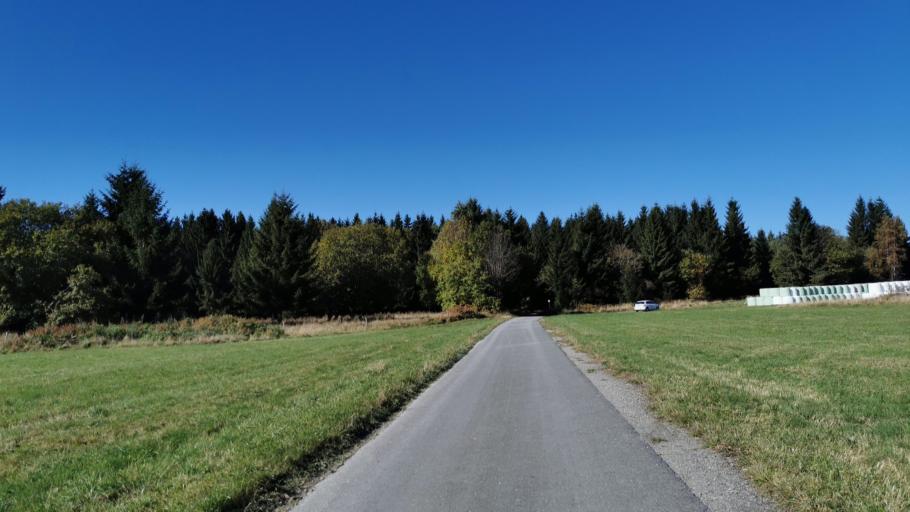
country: DE
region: Bavaria
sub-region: Upper Franconia
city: Tettau
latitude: 50.4839
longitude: 11.2928
